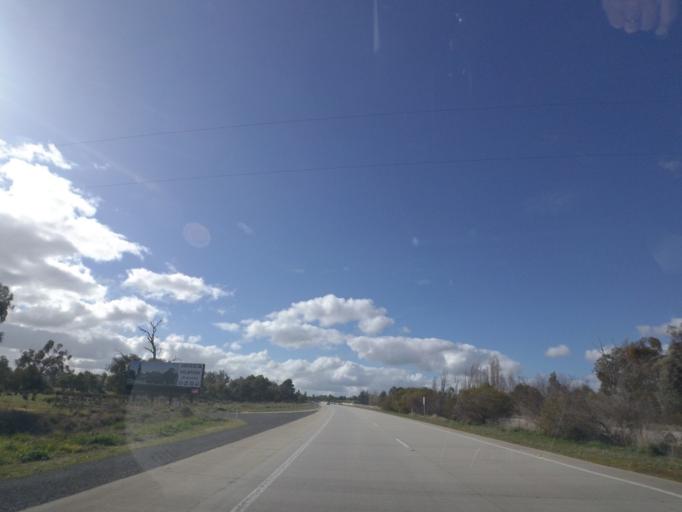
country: AU
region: New South Wales
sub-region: Greater Hume Shire
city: Holbrook
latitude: -35.9033
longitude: 147.1634
